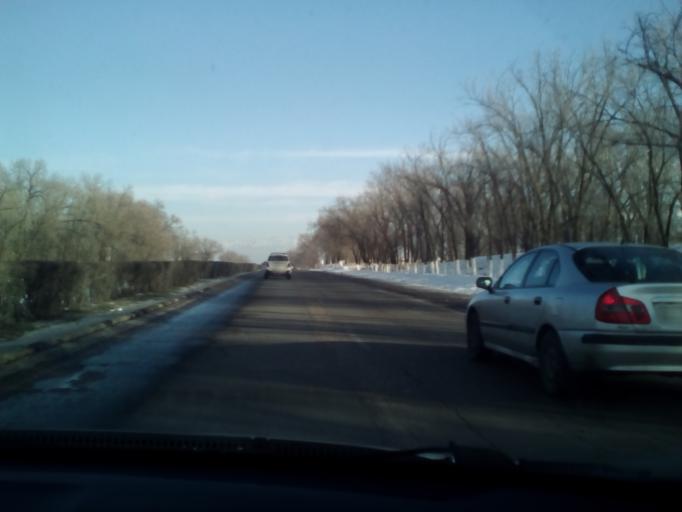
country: KZ
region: Almaty Oblysy
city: Burunday
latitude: 43.2211
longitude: 76.4479
